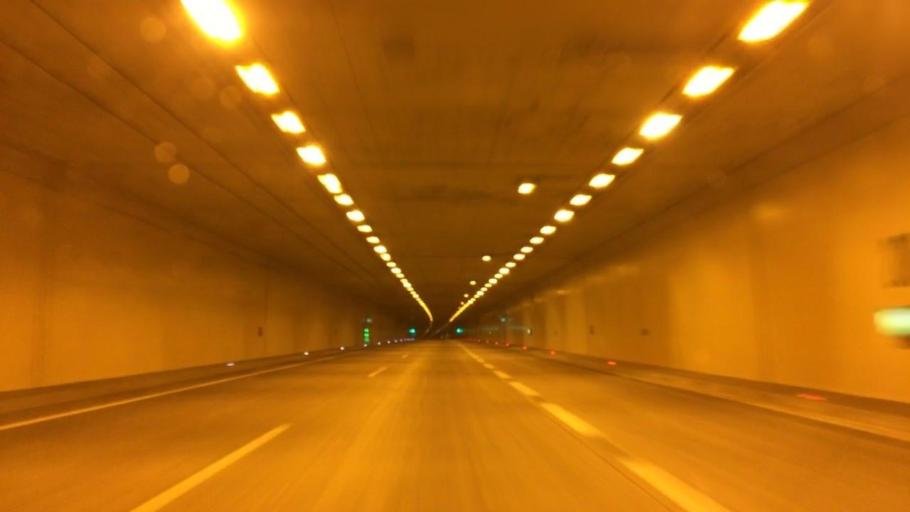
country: AT
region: Lower Austria
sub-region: Politischer Bezirk Korneuburg
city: Harmannsdorf
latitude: 48.3640
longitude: 16.3616
